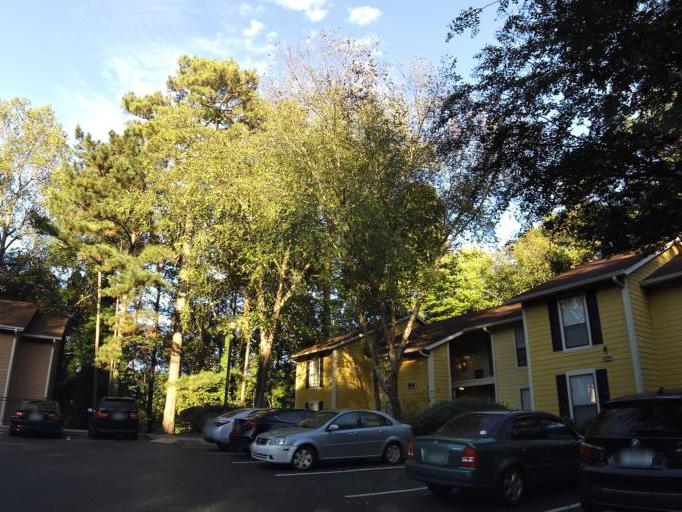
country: US
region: Georgia
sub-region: Cobb County
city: Vinings
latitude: 33.9063
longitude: -84.4497
